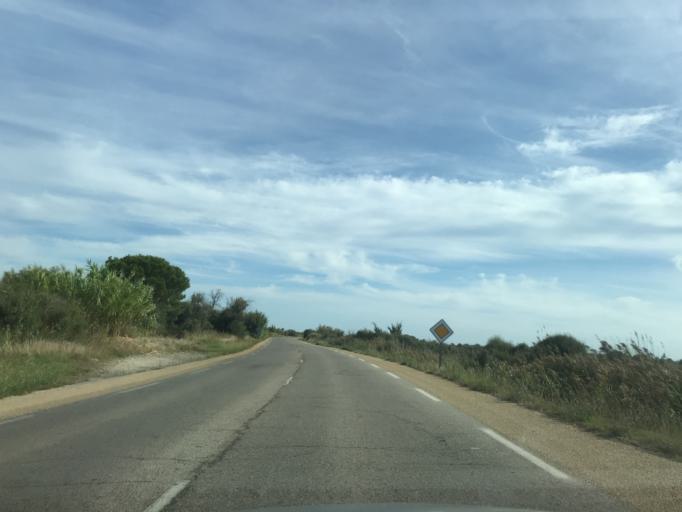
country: FR
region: Provence-Alpes-Cote d'Azur
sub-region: Departement des Bouches-du-Rhone
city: Saintes-Maries-de-la-Mer
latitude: 43.5034
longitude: 4.4010
